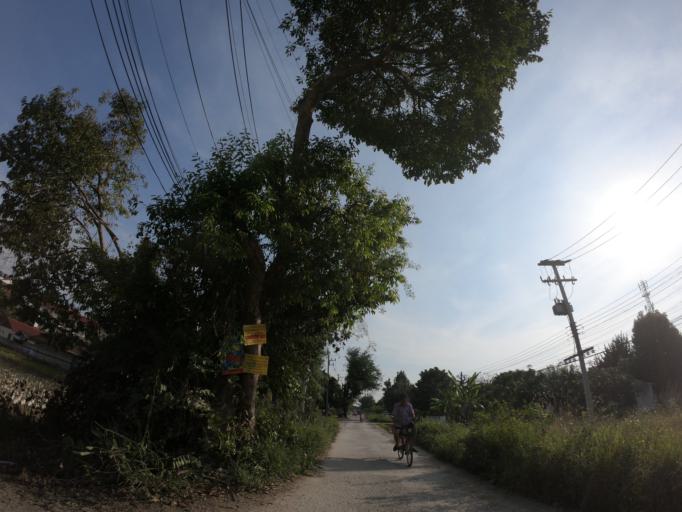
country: TH
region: Chiang Mai
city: Chiang Mai
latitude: 18.8258
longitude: 98.9930
